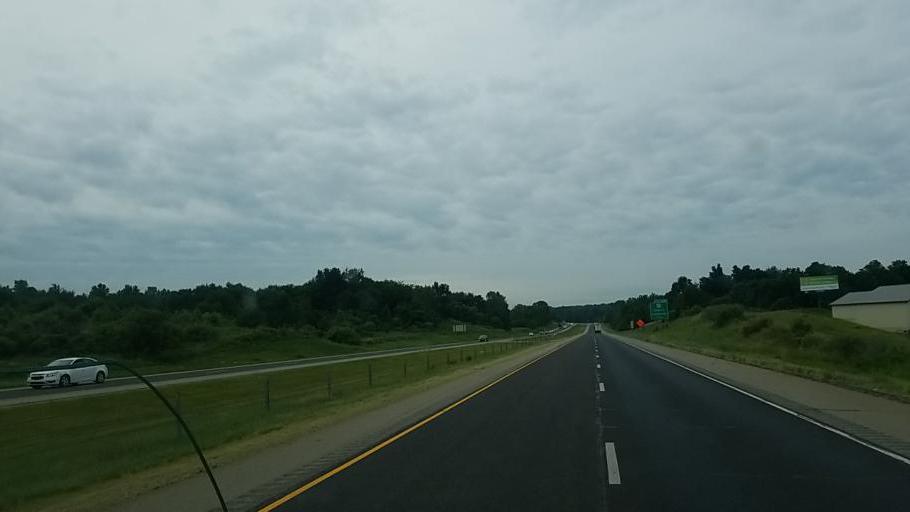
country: US
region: Indiana
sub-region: Steuben County
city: Angola
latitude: 41.6557
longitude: -85.0410
